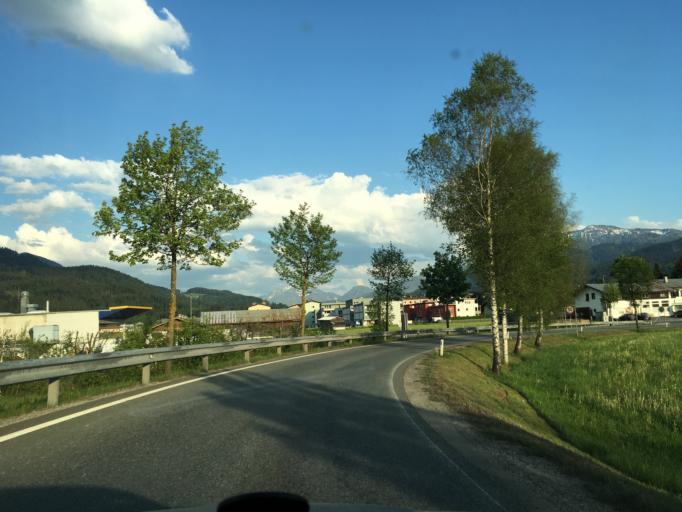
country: AT
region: Tyrol
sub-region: Politischer Bezirk Kitzbuhel
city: Sankt Johann in Tirol
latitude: 47.5297
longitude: 12.4328
